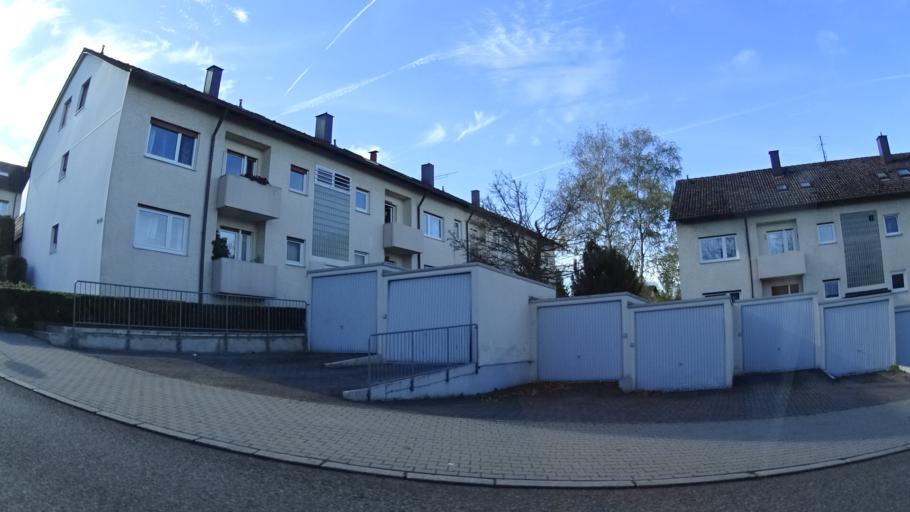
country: DE
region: Baden-Wuerttemberg
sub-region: Karlsruhe Region
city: Pforzheim
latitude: 48.8824
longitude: 8.7137
